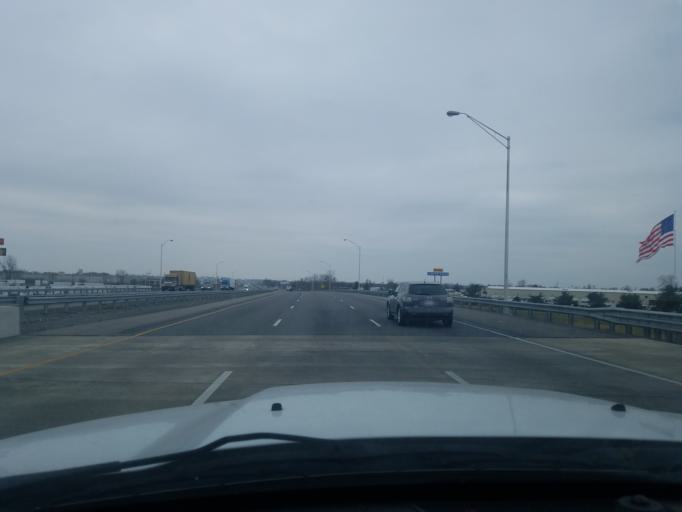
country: US
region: Indiana
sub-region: Johnson County
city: Greenwood
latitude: 39.6144
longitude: -86.0739
